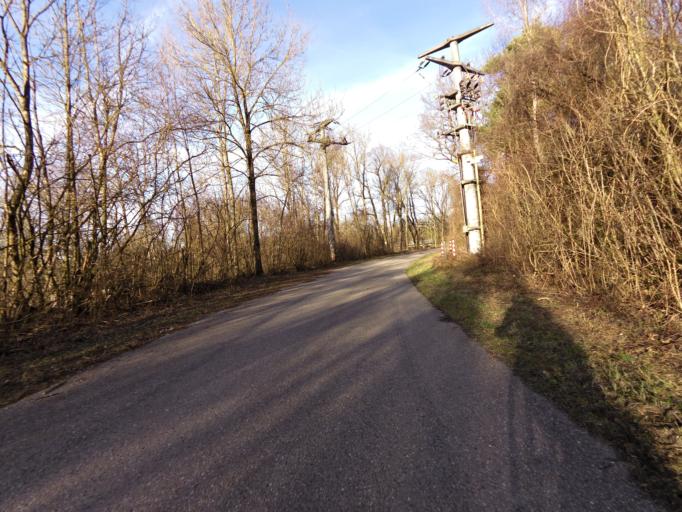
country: DE
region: Bavaria
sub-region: Upper Bavaria
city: Wang
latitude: 48.4878
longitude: 11.9762
